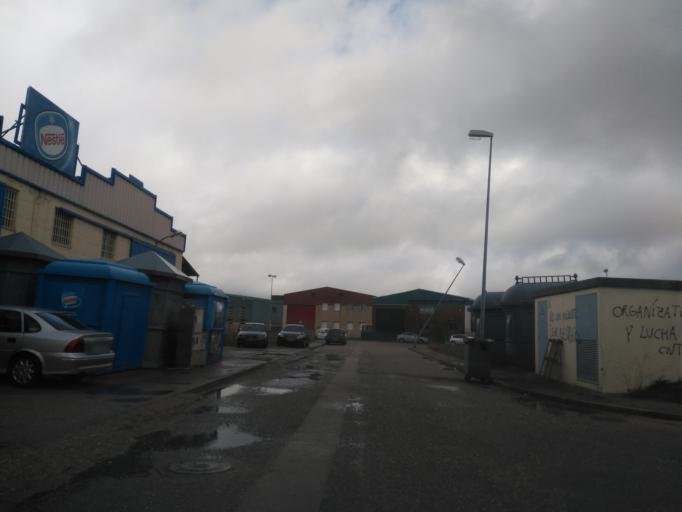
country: ES
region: Castille and Leon
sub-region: Provincia de Zamora
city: Morales del Vino
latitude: 41.4517
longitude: -5.7308
